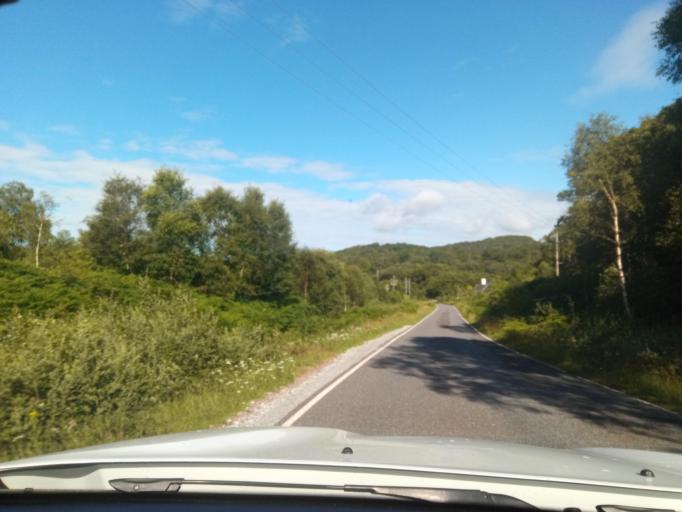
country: GB
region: Scotland
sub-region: Argyll and Bute
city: Isle Of Mull
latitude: 56.6877
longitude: -5.6609
